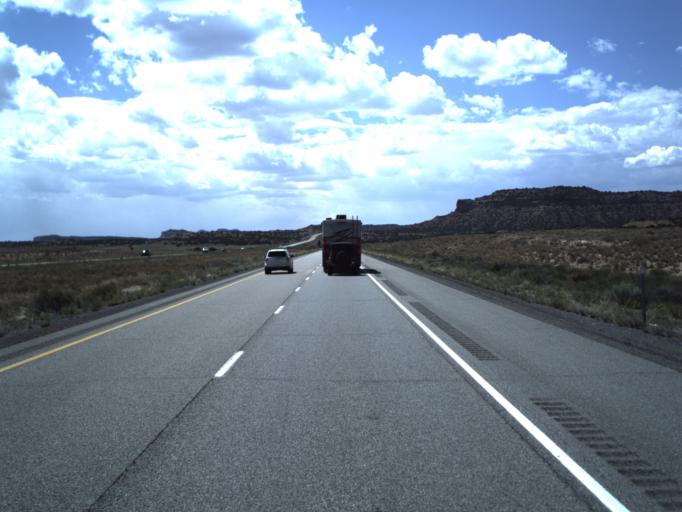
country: US
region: Utah
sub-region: Emery County
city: Castle Dale
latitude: 38.8731
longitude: -110.6822
